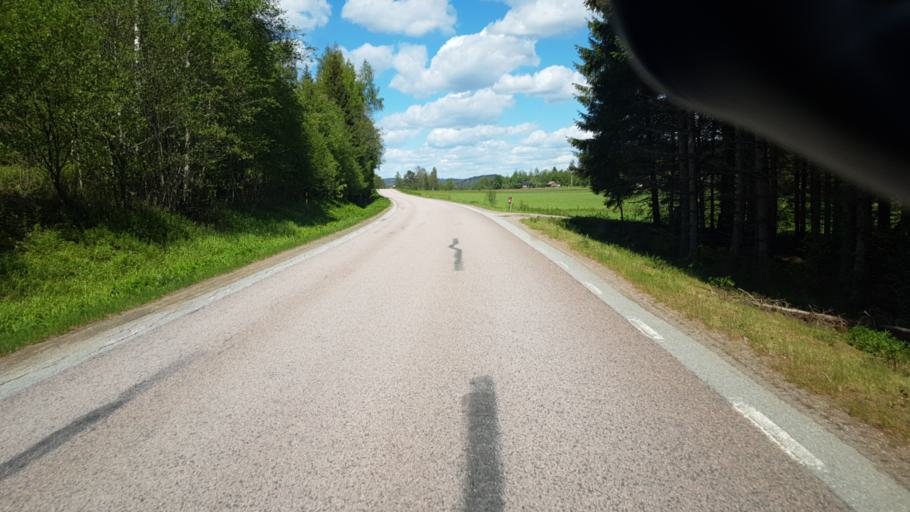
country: SE
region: Vaermland
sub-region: Arvika Kommun
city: Arvika
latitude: 59.7194
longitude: 12.7978
